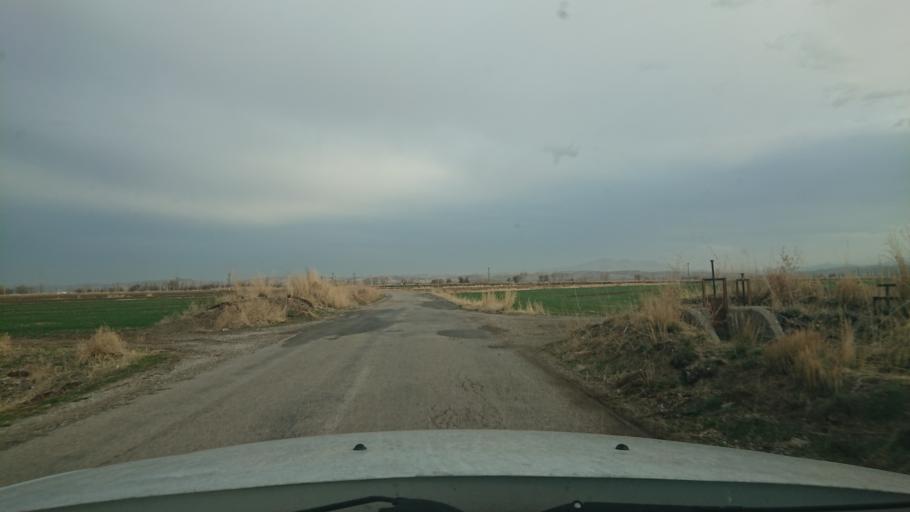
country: TR
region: Aksaray
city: Yesilova
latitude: 38.4348
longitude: 33.8376
